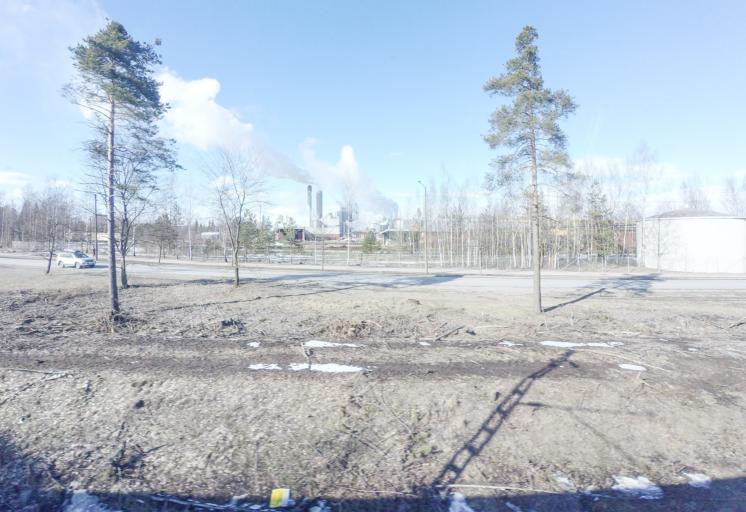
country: FI
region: South Karelia
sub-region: Lappeenranta
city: Lappeenranta
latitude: 61.0602
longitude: 28.2445
